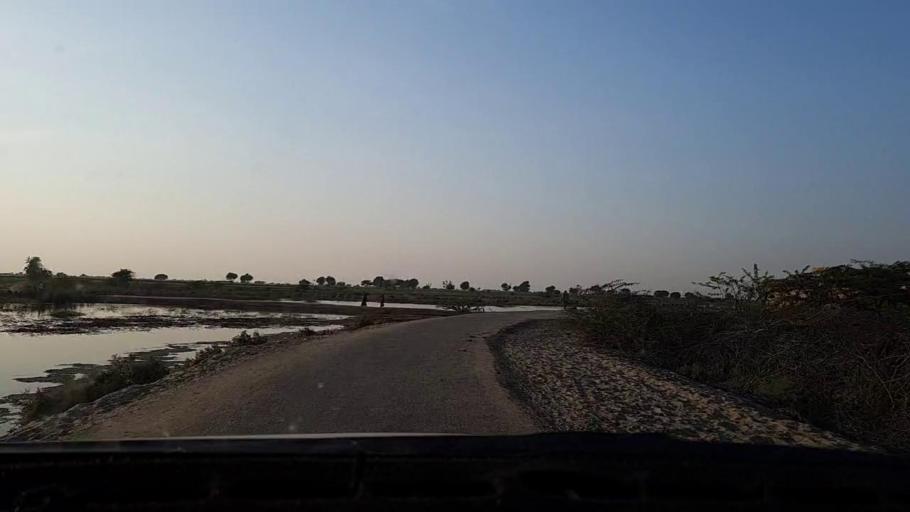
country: PK
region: Sindh
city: Tando Mittha Khan
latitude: 25.8664
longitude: 69.2656
